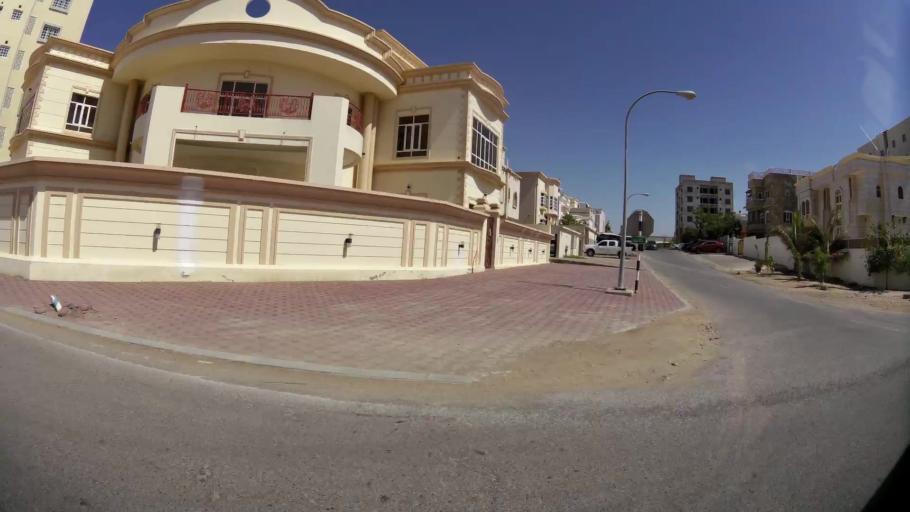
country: OM
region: Muhafazat Masqat
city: Bawshar
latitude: 23.5923
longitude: 58.3590
